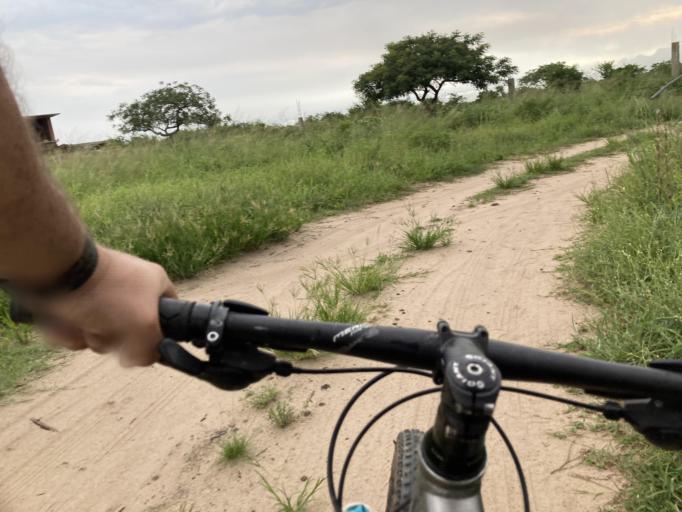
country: MZ
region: Maputo City
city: Maputo
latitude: -26.0530
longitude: 32.5343
